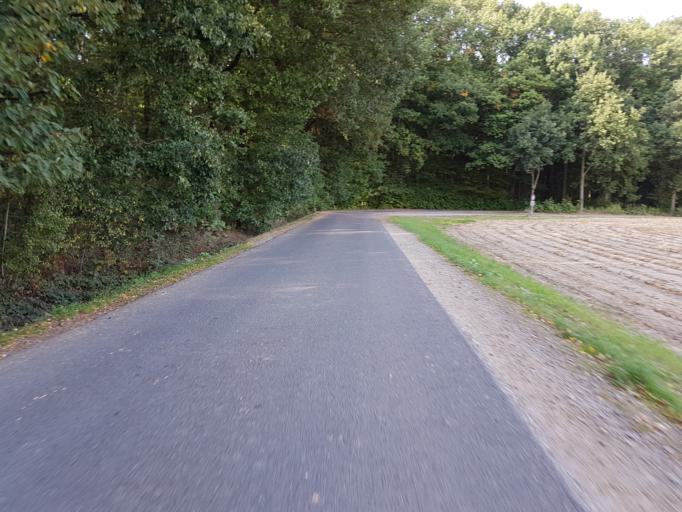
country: DE
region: Saxony
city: Claussnitz
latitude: 50.9499
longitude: 12.8795
